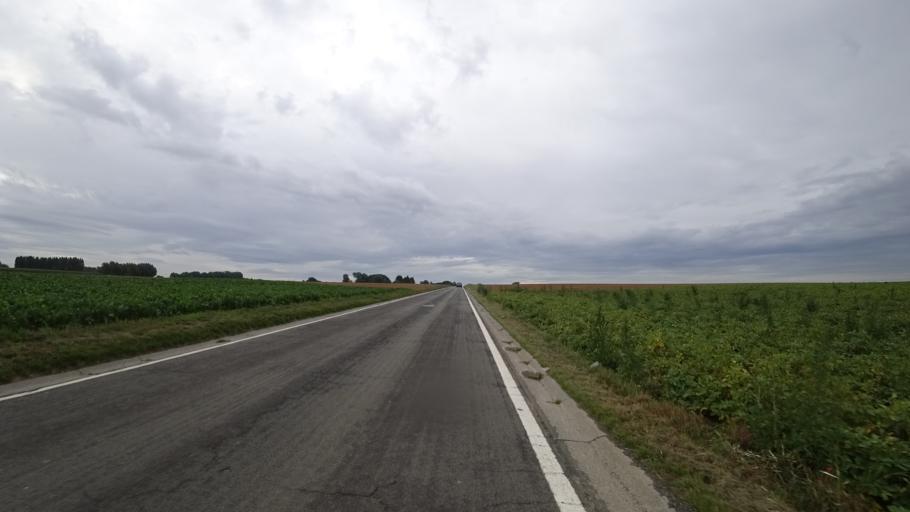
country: BE
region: Wallonia
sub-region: Province du Brabant Wallon
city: Perwez
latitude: 50.5914
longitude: 4.7591
